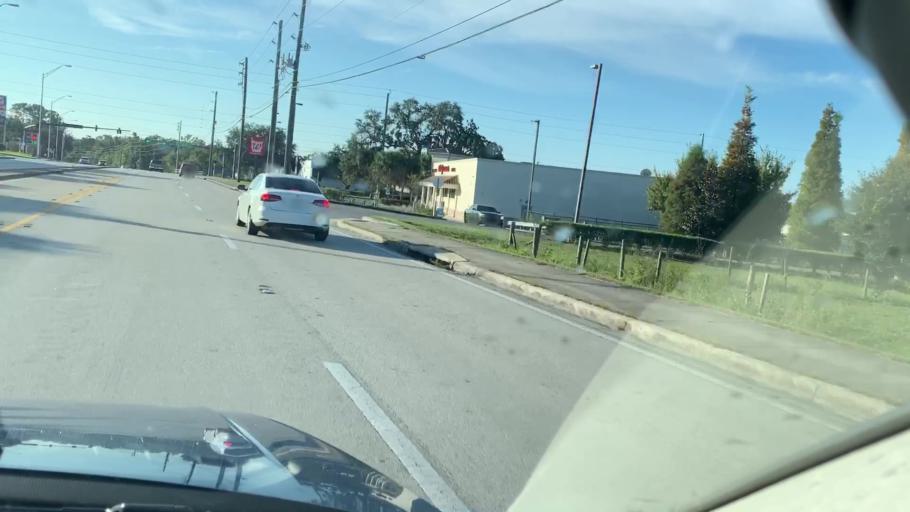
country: US
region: Florida
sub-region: Polk County
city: Gibsonia
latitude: 28.0820
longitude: -81.9948
